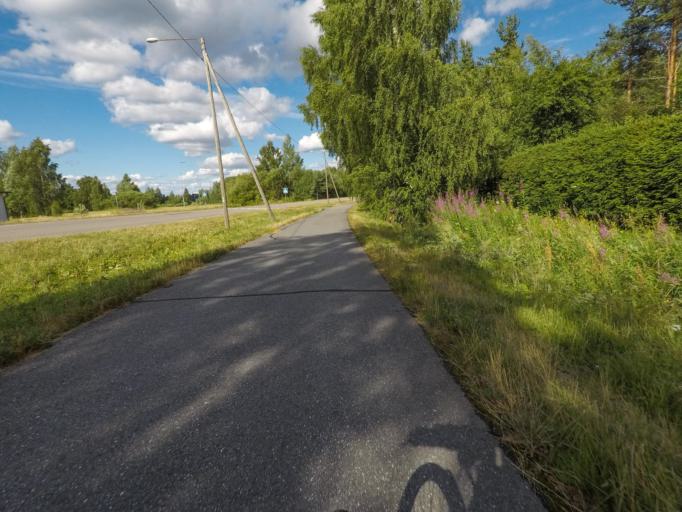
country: FI
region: South Karelia
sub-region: Lappeenranta
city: Joutseno
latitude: 61.1271
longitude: 28.4967
